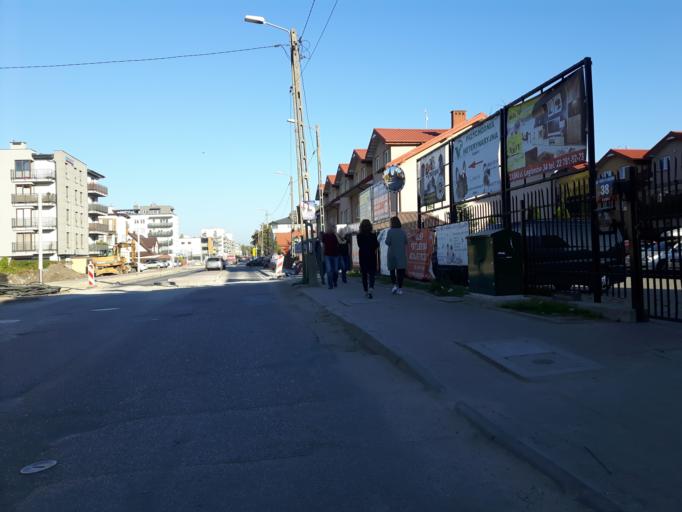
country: PL
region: Masovian Voivodeship
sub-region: Powiat wolominski
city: Zabki
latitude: 52.2795
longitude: 21.1278
